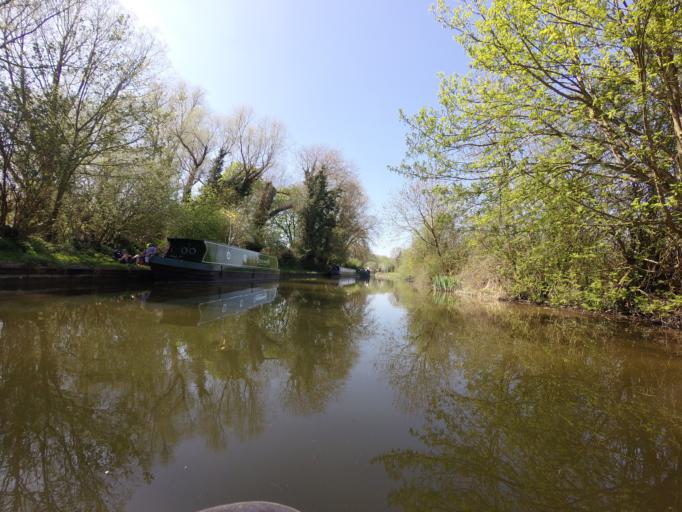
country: GB
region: England
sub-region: Hertfordshire
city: Berkhamsted
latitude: 51.7772
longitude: -0.5988
